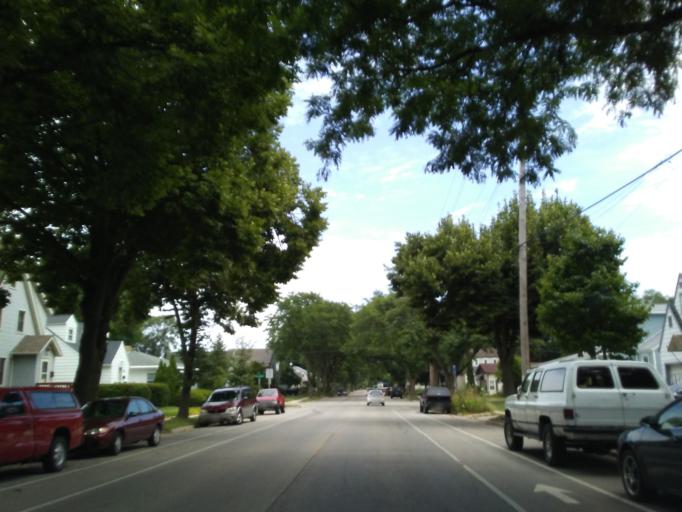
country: US
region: Wisconsin
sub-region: Dane County
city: Maple Bluff
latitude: 43.1068
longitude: -89.3464
